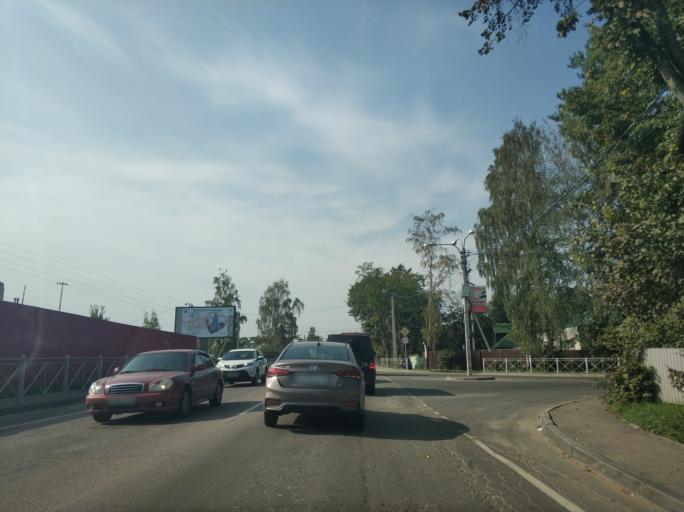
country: RU
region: Leningrad
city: Murino
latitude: 60.0463
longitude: 30.4535
